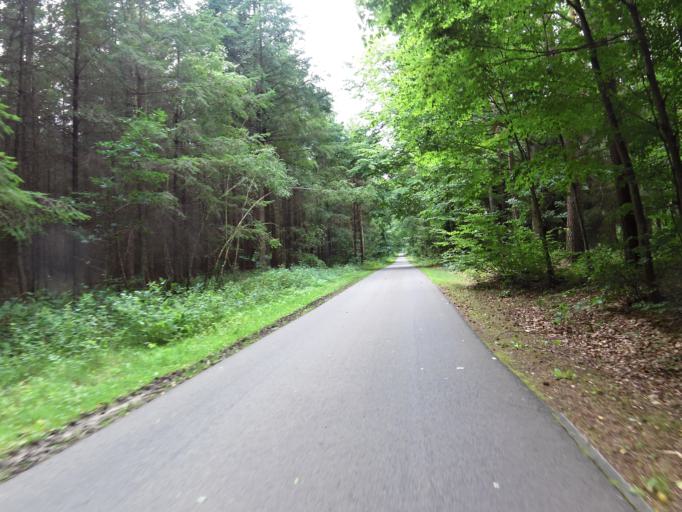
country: DE
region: Brandenburg
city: Templin
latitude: 53.1621
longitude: 13.4389
